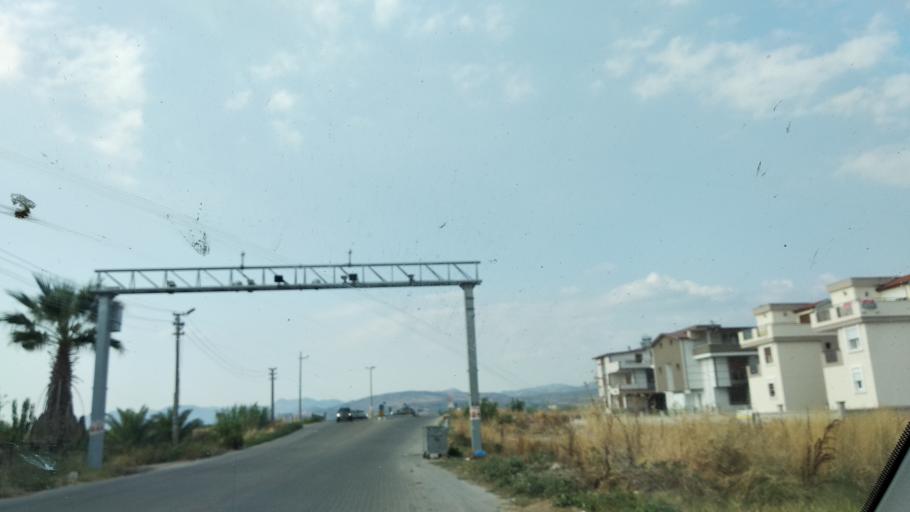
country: TR
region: Izmir
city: Dikili
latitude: 39.1033
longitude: 26.8828
